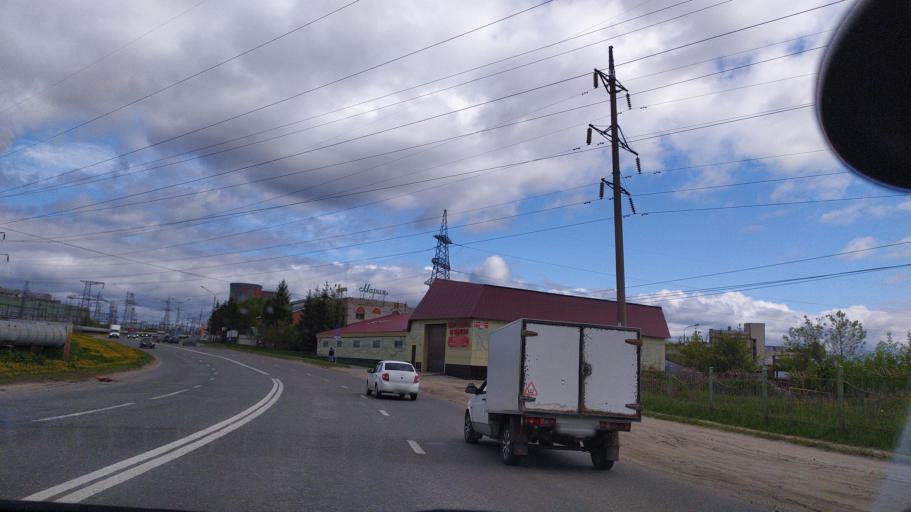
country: RU
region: Chuvashia
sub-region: Cheboksarskiy Rayon
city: Cheboksary
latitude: 56.1173
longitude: 47.3016
